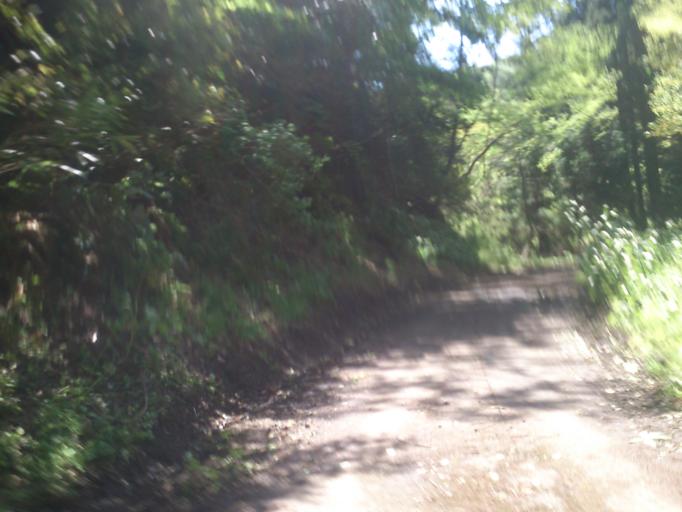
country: JP
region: Kyoto
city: Miyazu
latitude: 35.7151
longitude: 135.1426
